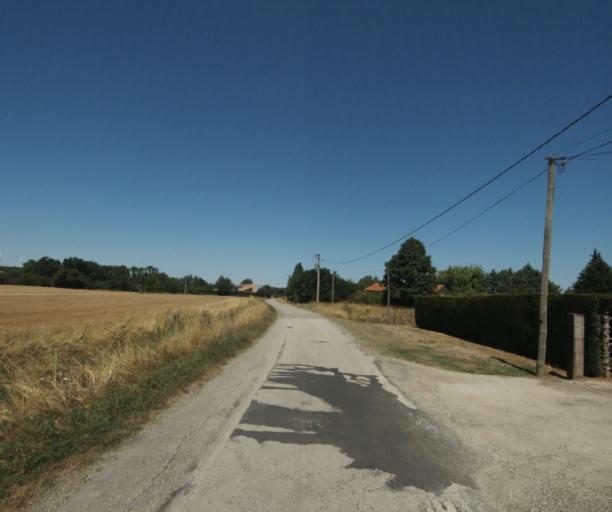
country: FR
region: Midi-Pyrenees
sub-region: Departement de la Haute-Garonne
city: Saint-Felix-Lauragais
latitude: 43.4486
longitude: 1.9375
